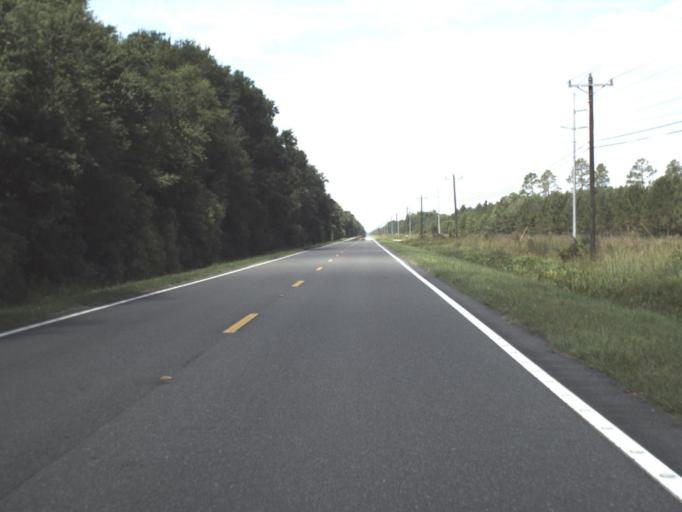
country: US
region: Florida
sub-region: Levy County
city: Chiefland
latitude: 29.2994
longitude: -82.8178
